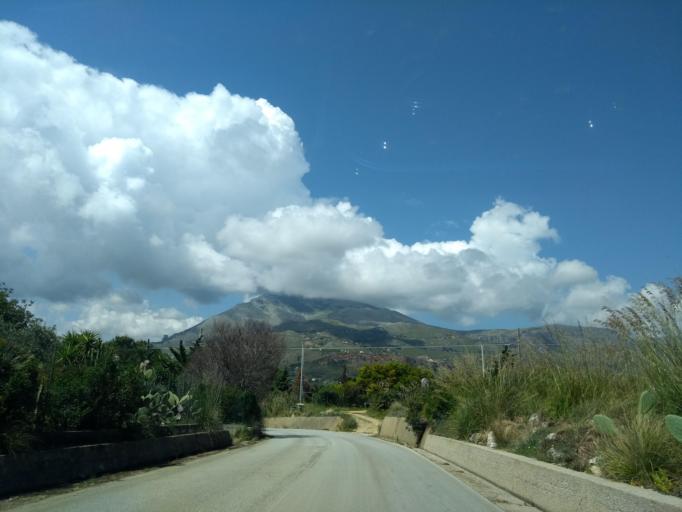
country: IT
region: Sicily
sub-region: Trapani
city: Castellammare del Golfo
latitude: 38.0449
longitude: 12.8474
